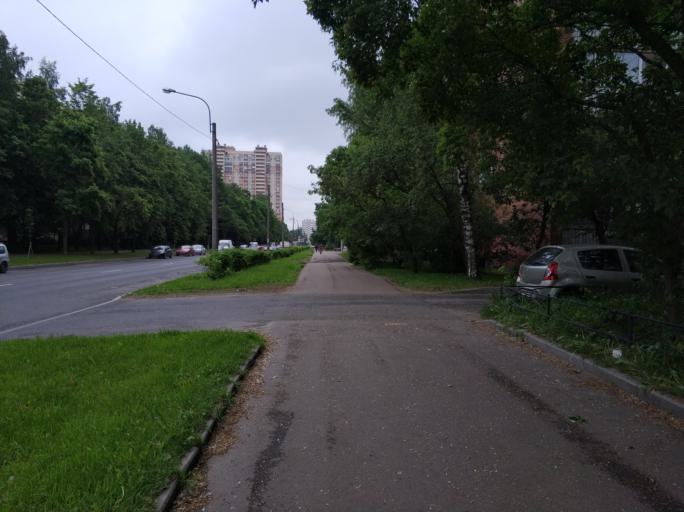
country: RU
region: St.-Petersburg
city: Grazhdanka
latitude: 60.0336
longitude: 30.3957
